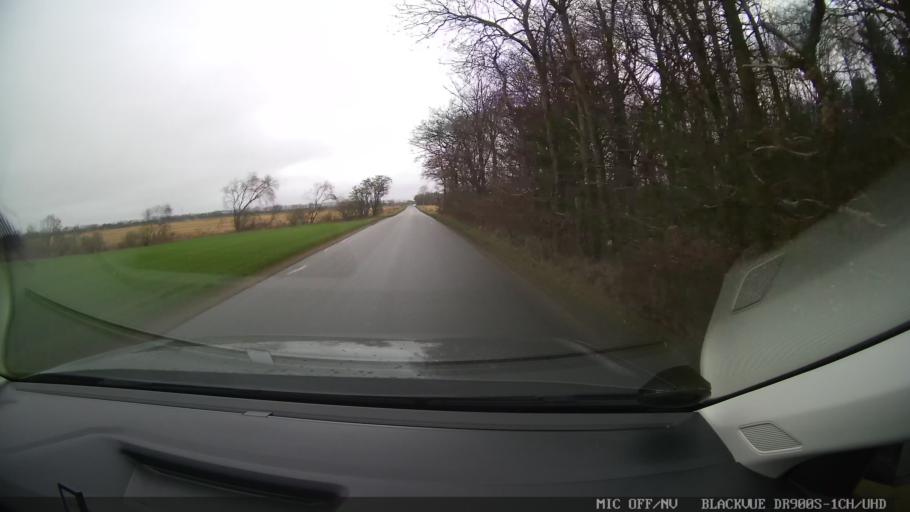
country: DK
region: Central Jutland
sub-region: Viborg Kommune
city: Karup
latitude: 56.3365
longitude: 9.2736
